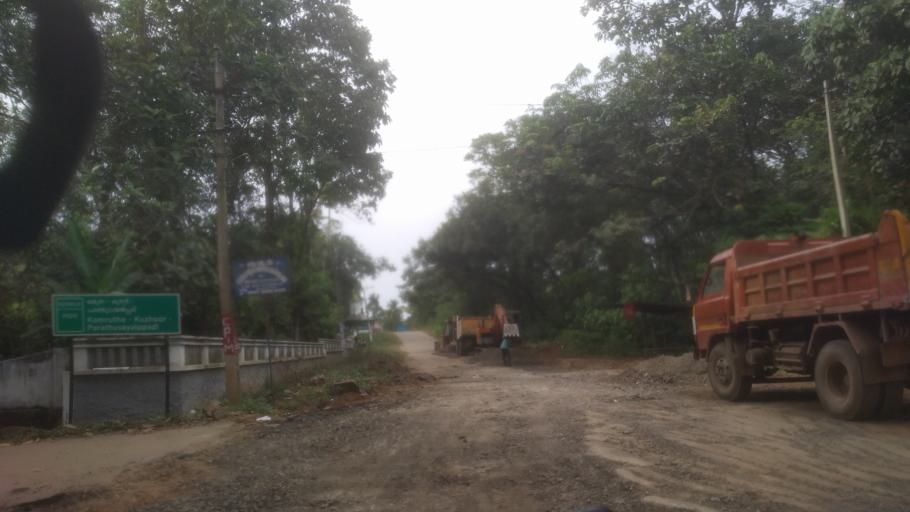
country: IN
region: Kerala
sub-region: Ernakulam
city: Perumbavoor
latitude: 10.0489
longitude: 76.5249
